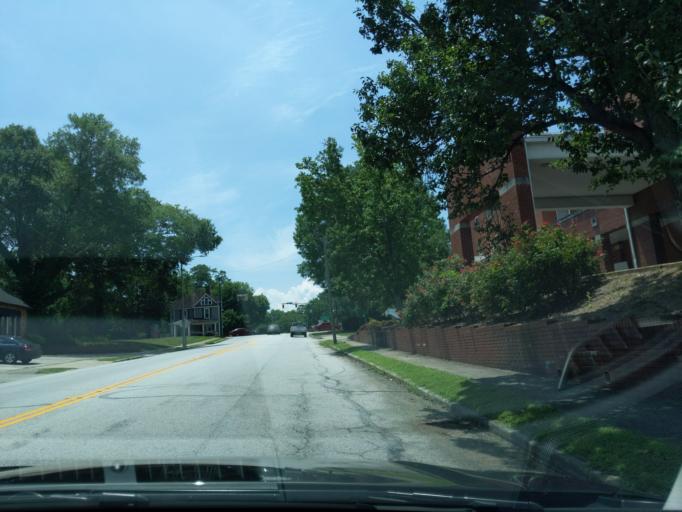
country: US
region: South Carolina
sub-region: Laurens County
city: Laurens
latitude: 34.4993
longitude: -82.0187
